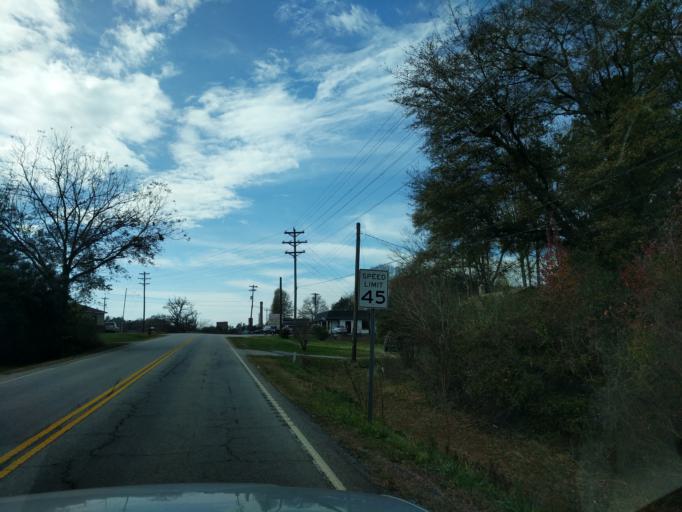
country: US
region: South Carolina
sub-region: Pickens County
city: Pickens
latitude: 34.8899
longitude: -82.6874
